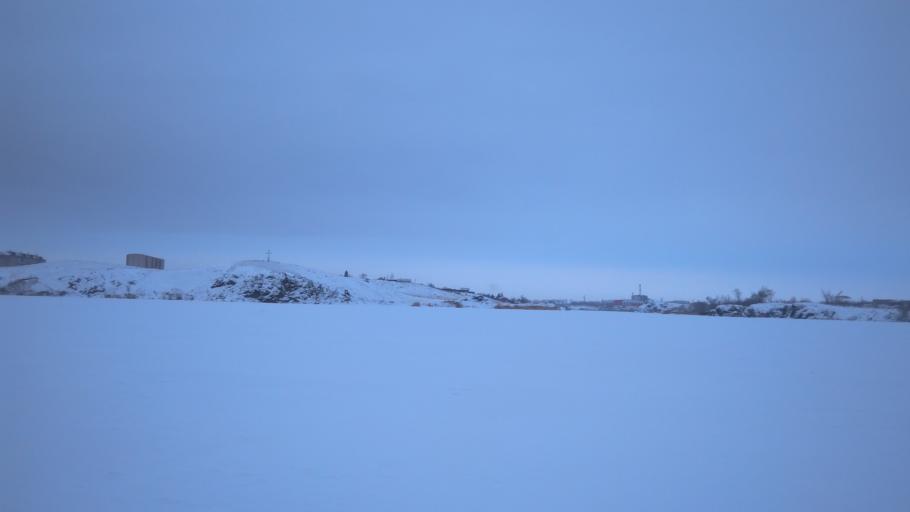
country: RU
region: Chelyabinsk
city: Troitsk
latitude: 54.0804
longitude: 61.5736
